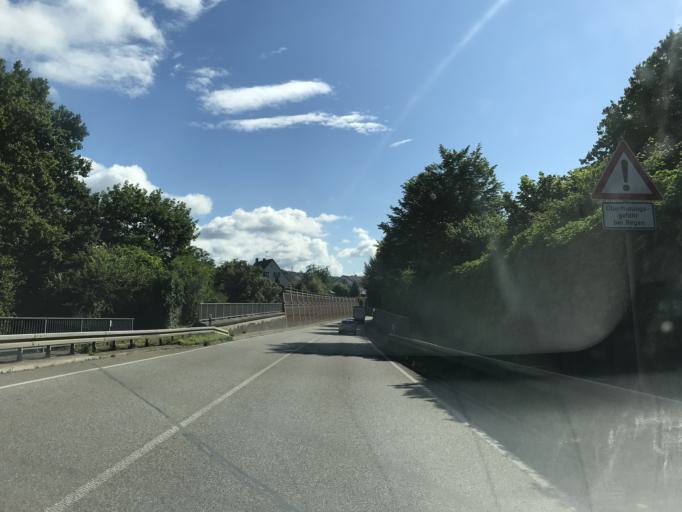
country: DE
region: Baden-Wuerttemberg
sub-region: Freiburg Region
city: Loerrach
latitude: 47.6390
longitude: 7.6923
